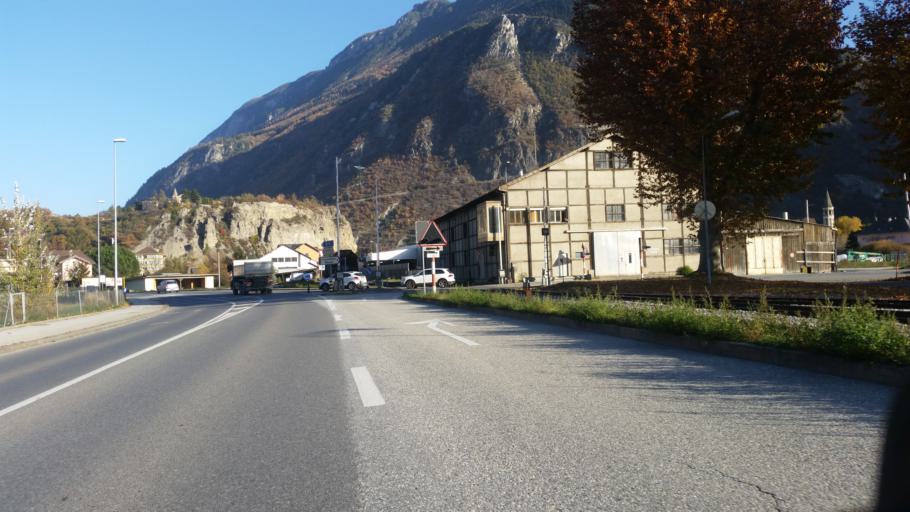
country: CH
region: Valais
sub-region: Sierre District
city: Sierre
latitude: 46.2840
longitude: 7.5342
